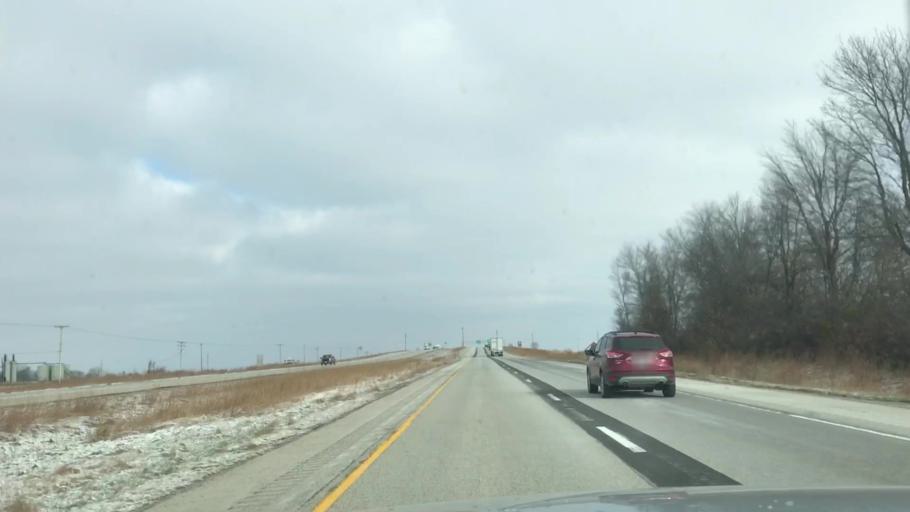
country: US
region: Illinois
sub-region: Sangamon County
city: Divernon
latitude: 39.5839
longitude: -89.6463
